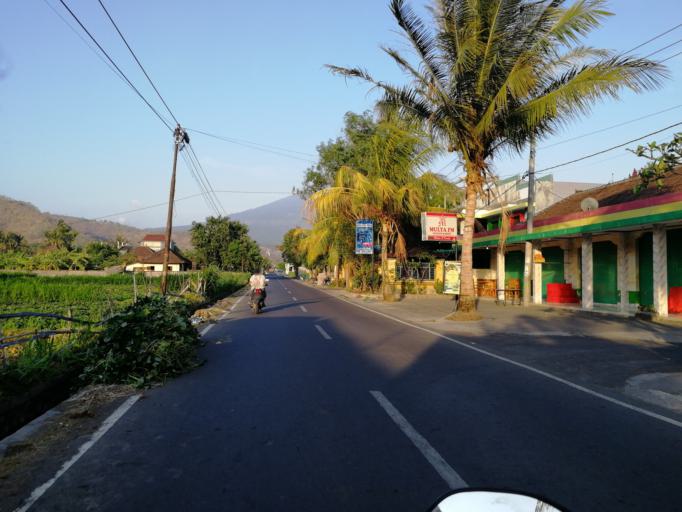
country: ID
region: Bali
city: Biaslantang Kaler
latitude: -8.3339
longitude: 115.6398
